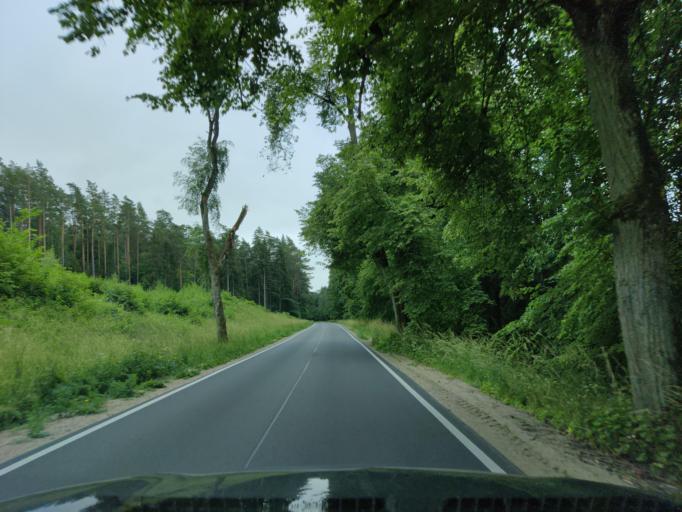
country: PL
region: Warmian-Masurian Voivodeship
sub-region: Powiat gizycki
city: Ryn
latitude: 53.8907
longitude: 21.5744
